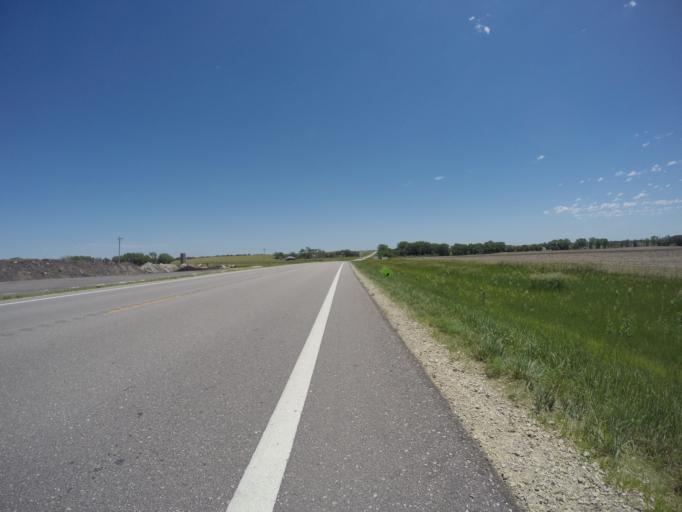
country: US
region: Kansas
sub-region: Republic County
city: Belleville
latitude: 39.8125
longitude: -97.6962
